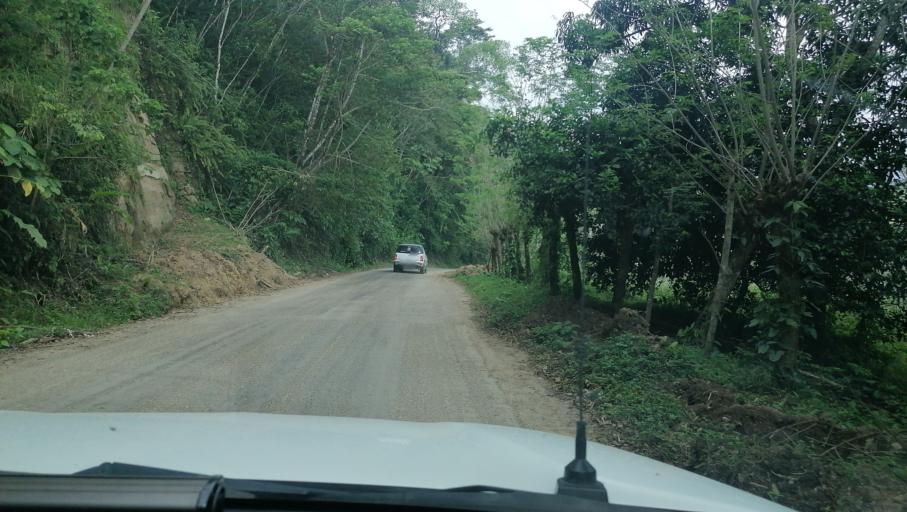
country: MX
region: Chiapas
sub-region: Francisco Leon
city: San Miguel la Sardina
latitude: 17.2289
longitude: -93.3433
